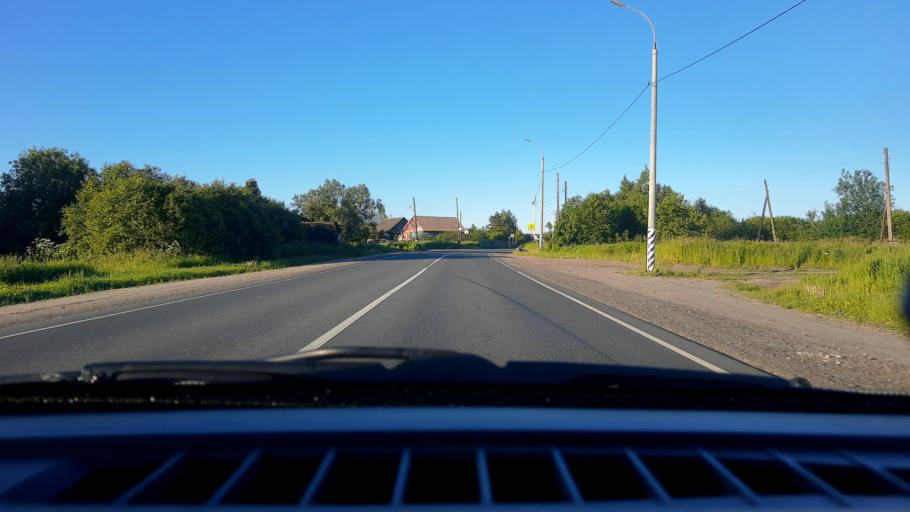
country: RU
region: Nizjnij Novgorod
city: Linda
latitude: 56.6029
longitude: 44.0446
